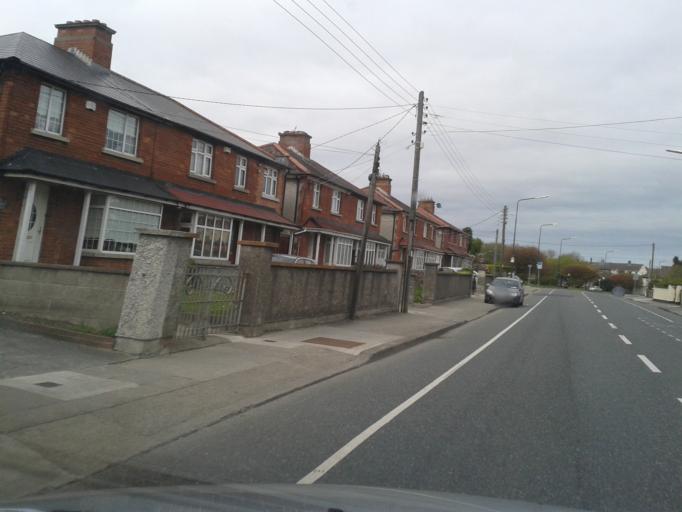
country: IE
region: Leinster
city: Beaumont
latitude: 53.3832
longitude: -6.2375
